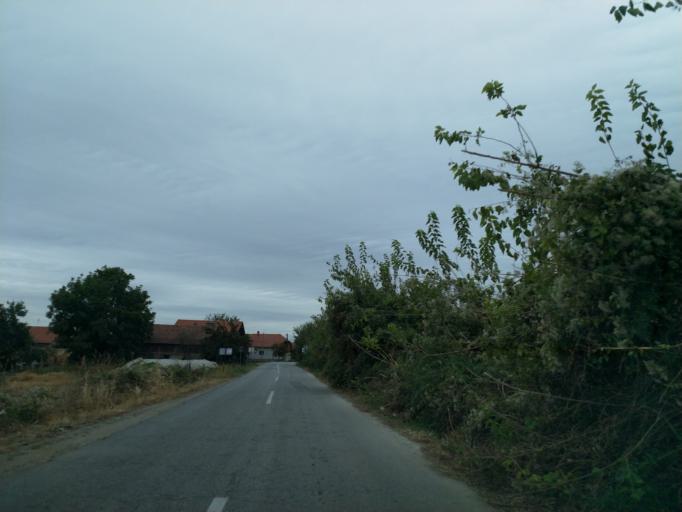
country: RS
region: Central Serbia
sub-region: Pomoravski Okrug
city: Paracin
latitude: 43.8442
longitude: 21.3224
